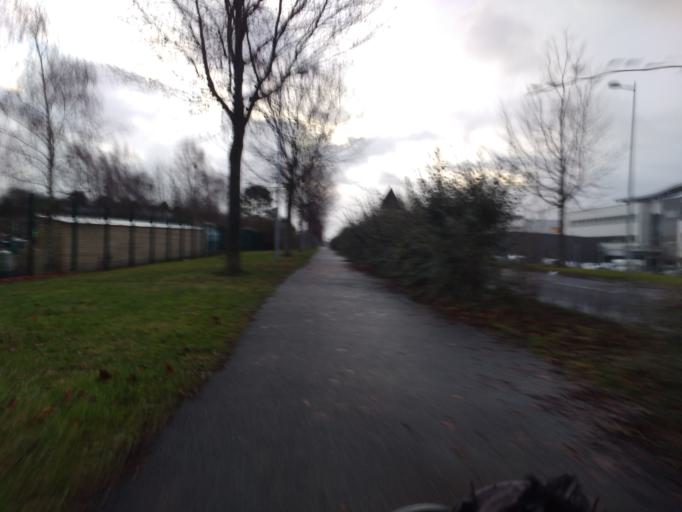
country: FR
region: Picardie
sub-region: Departement de la Somme
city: Longueau
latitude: 49.8661
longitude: 2.3692
